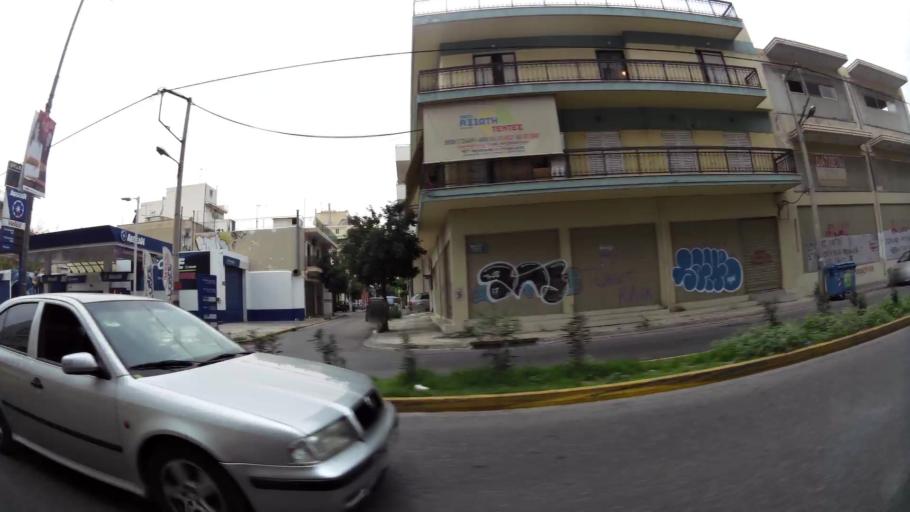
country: GR
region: Attica
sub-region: Nomos Piraios
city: Agios Ioannis Rentis
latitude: 37.9675
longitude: 23.6619
